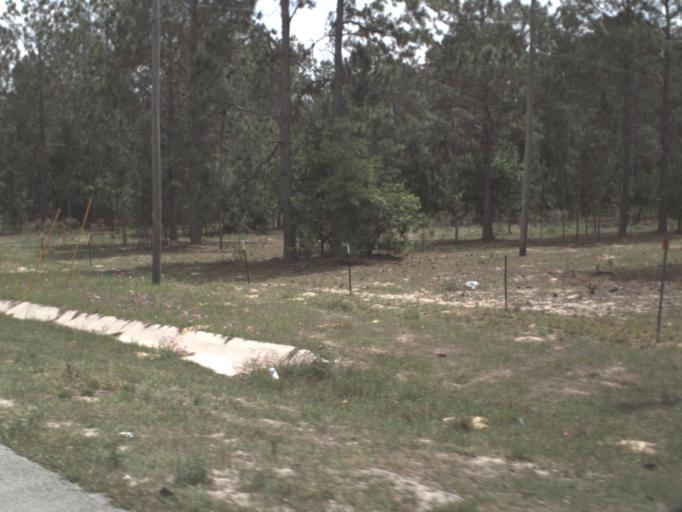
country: US
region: Florida
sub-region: Lake County
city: Mount Plymouth
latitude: 28.8517
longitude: -81.5427
